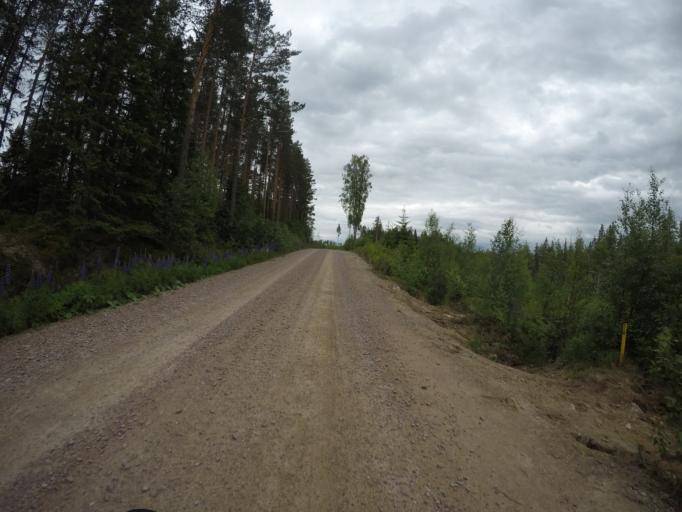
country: SE
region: Dalarna
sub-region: Ludvika Kommun
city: Abborrberget
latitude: 60.1028
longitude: 14.5279
